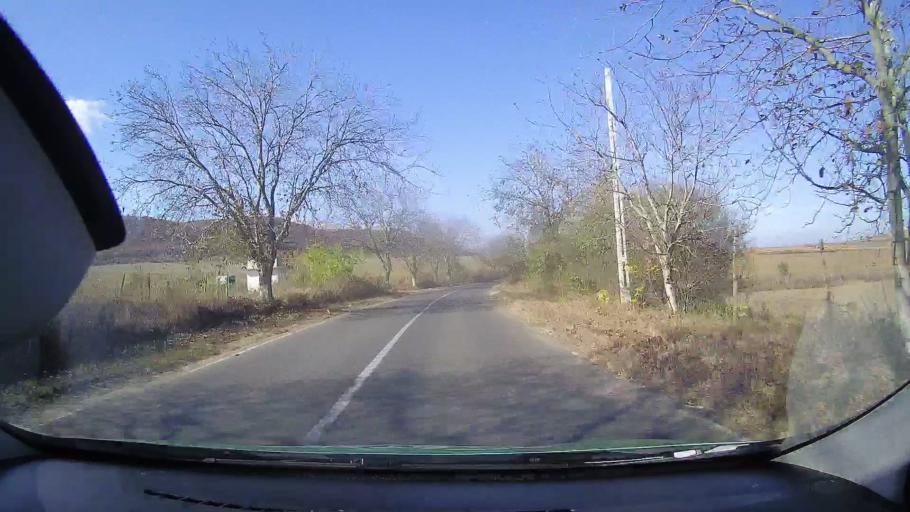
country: RO
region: Tulcea
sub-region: Oras Babadag
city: Babadag
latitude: 44.8804
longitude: 28.7469
